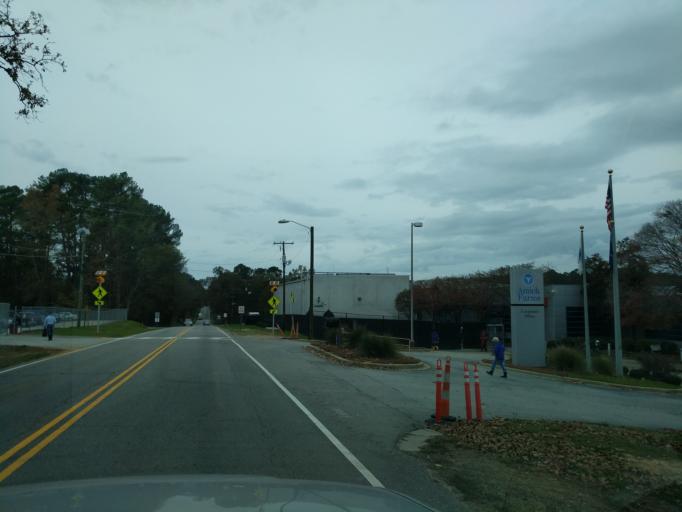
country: US
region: South Carolina
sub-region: Lexington County
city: Batesburg
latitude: 33.9560
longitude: -81.6381
